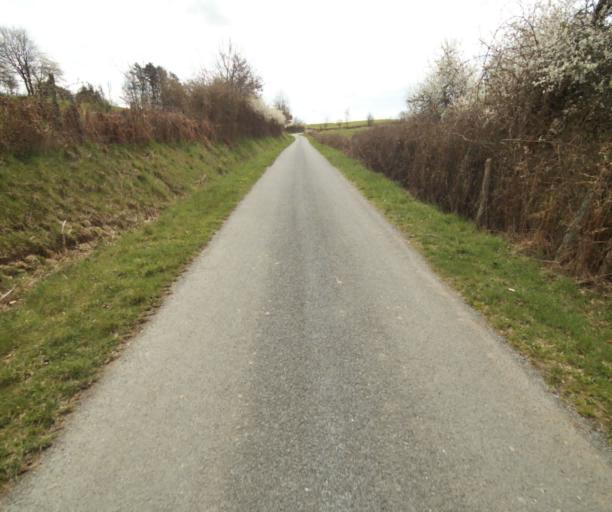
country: FR
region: Limousin
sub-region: Departement de la Correze
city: Correze
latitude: 45.3806
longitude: 1.9634
